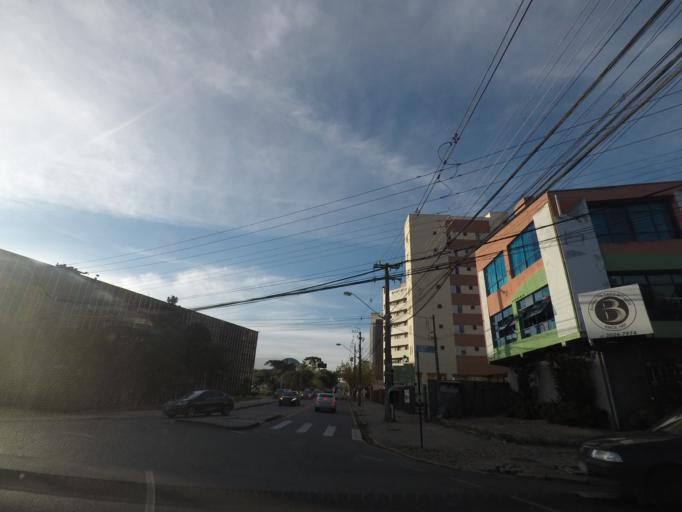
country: BR
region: Parana
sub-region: Curitiba
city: Curitiba
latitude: -25.4126
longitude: -49.2657
